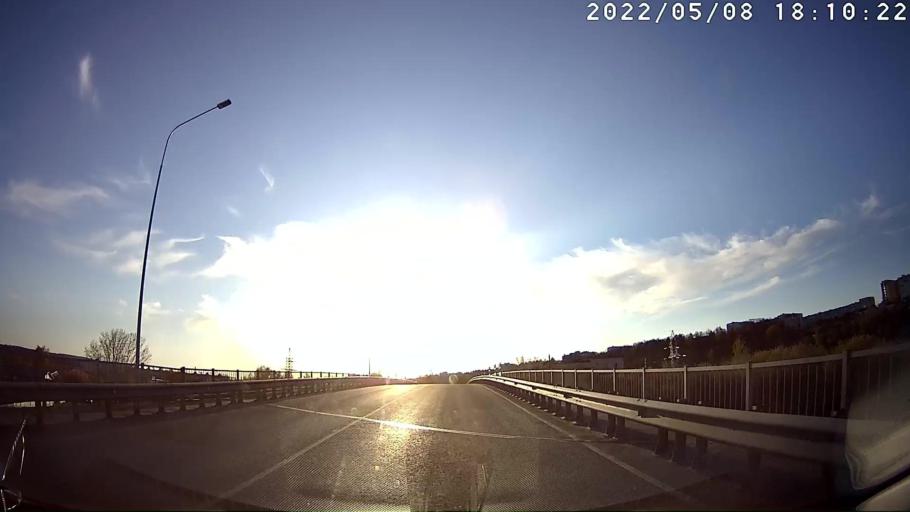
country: RU
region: Tatarstan
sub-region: Zelenodol'skiy Rayon
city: Zelenodolsk
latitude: 55.8386
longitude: 48.5258
